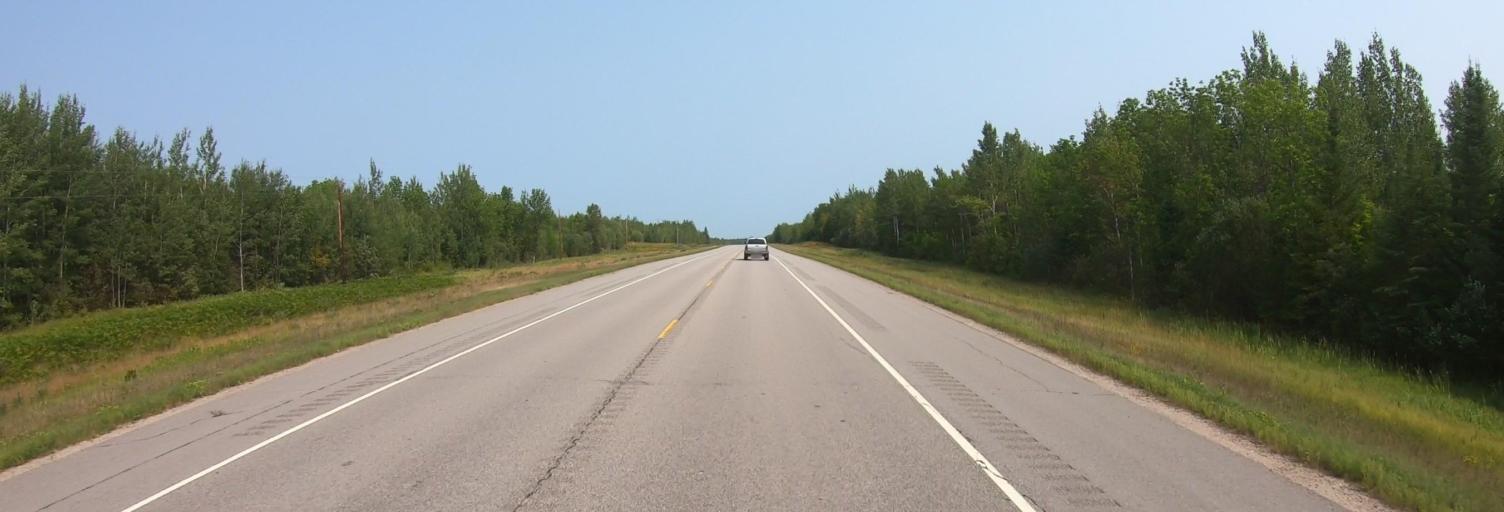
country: CA
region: Ontario
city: Fort Frances
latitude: 48.3065
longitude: -92.9671
